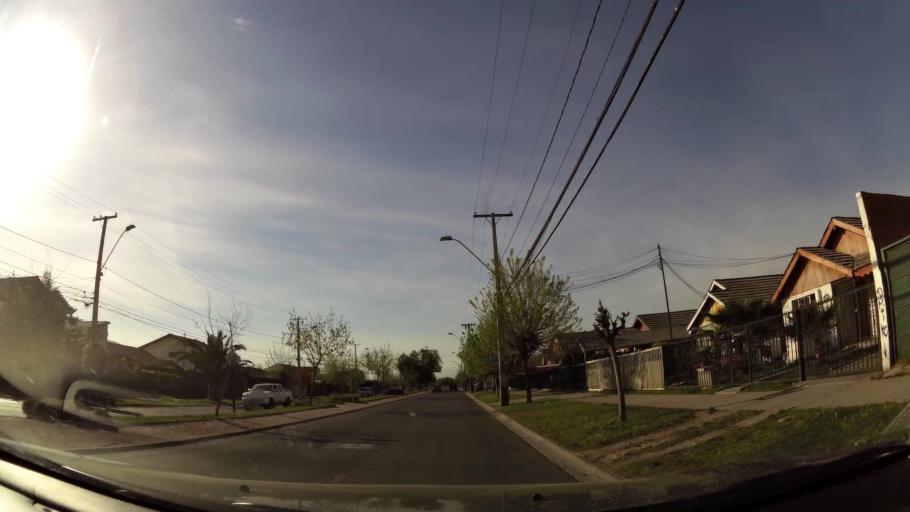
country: CL
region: Santiago Metropolitan
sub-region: Provincia de Cordillera
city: Puente Alto
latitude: -33.5831
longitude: -70.5634
